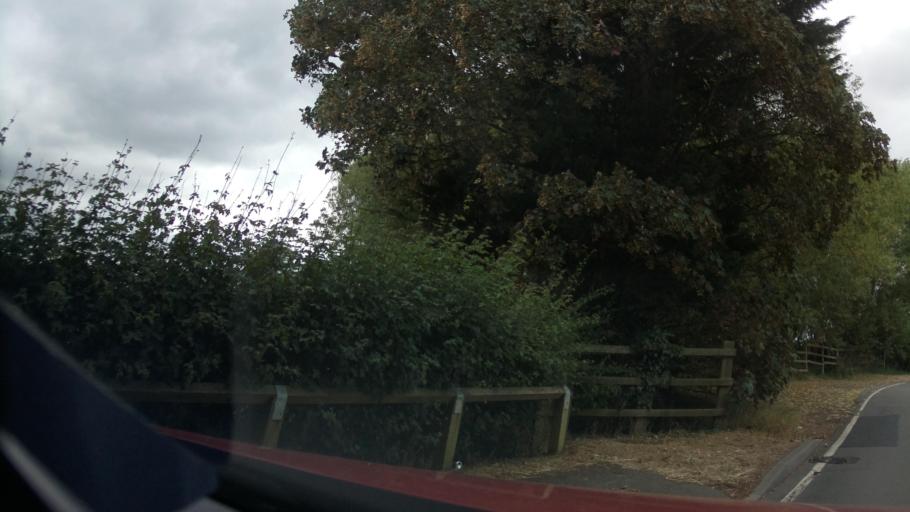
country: GB
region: England
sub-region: Derbyshire
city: Long Eaton
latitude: 52.9051
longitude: -1.3183
